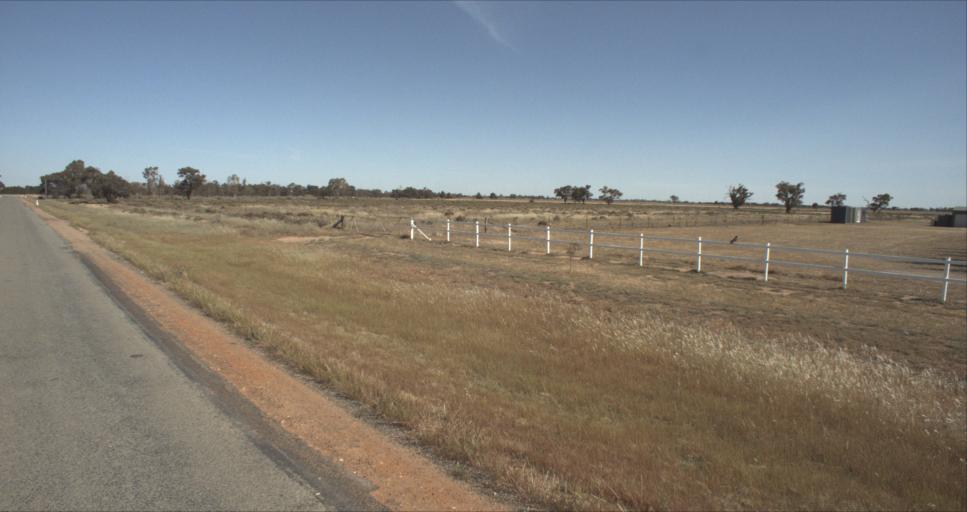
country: AU
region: New South Wales
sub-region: Leeton
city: Leeton
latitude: -34.4974
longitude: 146.3909
